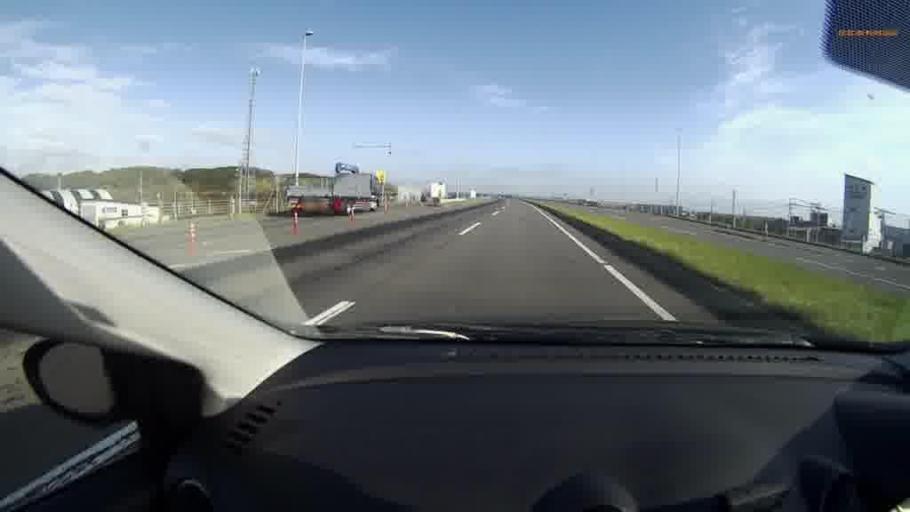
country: JP
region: Hokkaido
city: Kushiro
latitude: 43.0064
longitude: 144.2553
